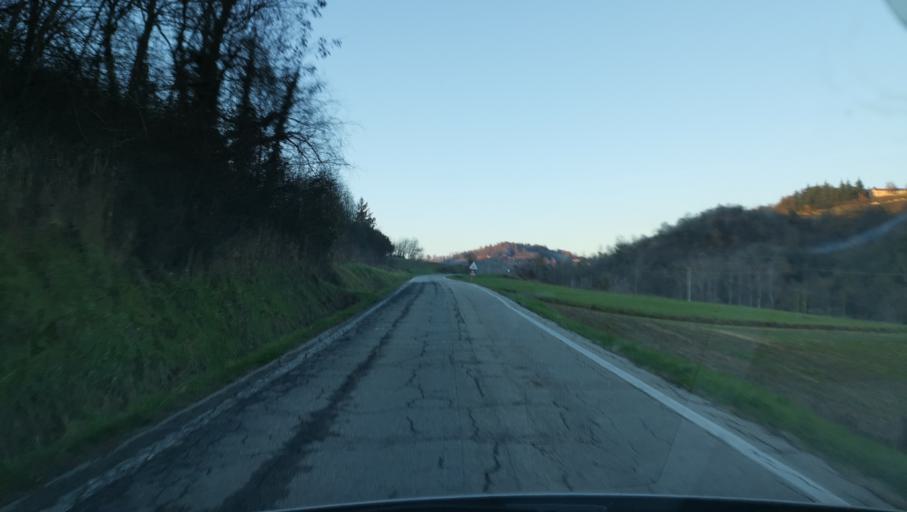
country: IT
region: Piedmont
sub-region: Provincia di Asti
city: Moncucco Torinese
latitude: 45.0734
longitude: 7.9409
